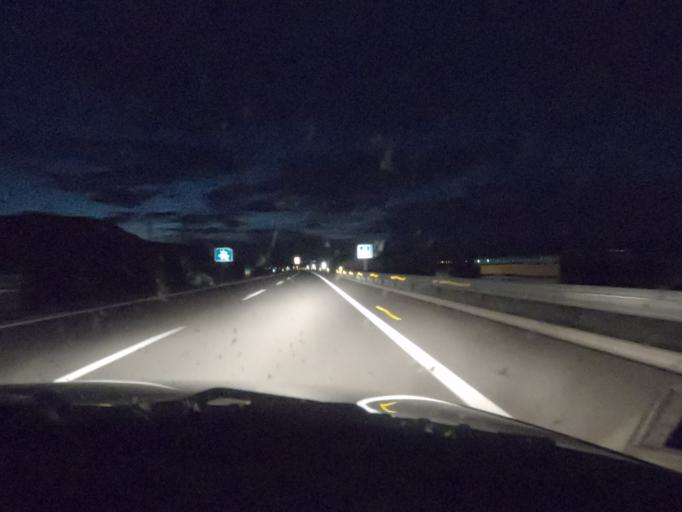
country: ES
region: Extremadura
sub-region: Provincia de Caceres
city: Casas de Don Gomez
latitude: 40.0231
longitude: -6.5989
